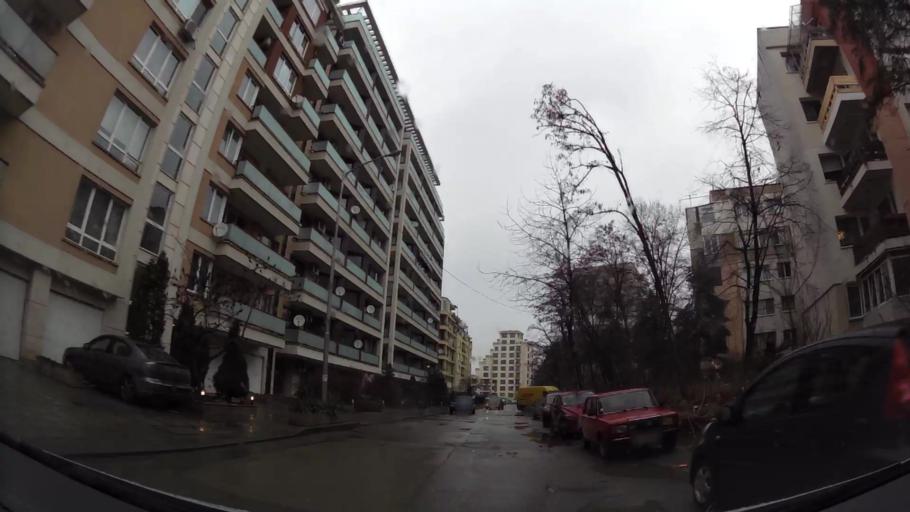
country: BG
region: Sofia-Capital
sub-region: Stolichna Obshtina
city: Sofia
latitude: 42.6388
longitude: 23.3660
